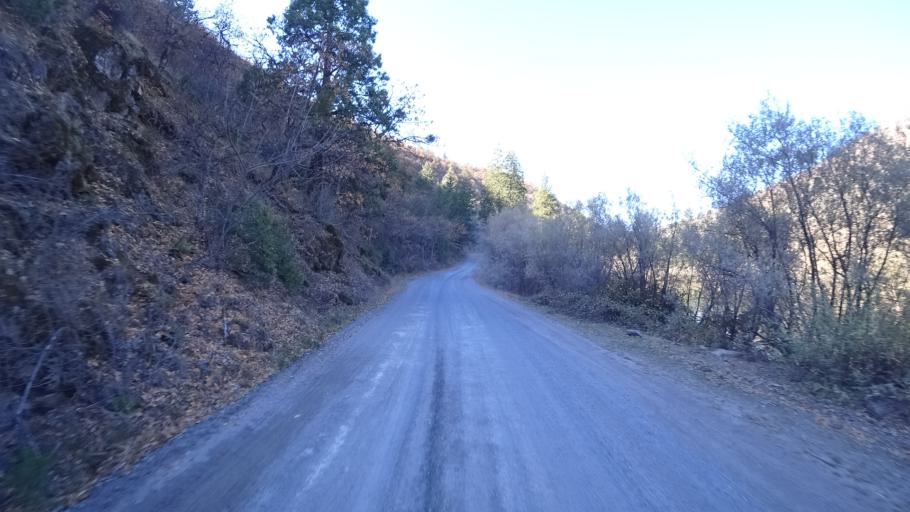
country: US
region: California
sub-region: Siskiyou County
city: Yreka
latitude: 41.8271
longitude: -122.6467
